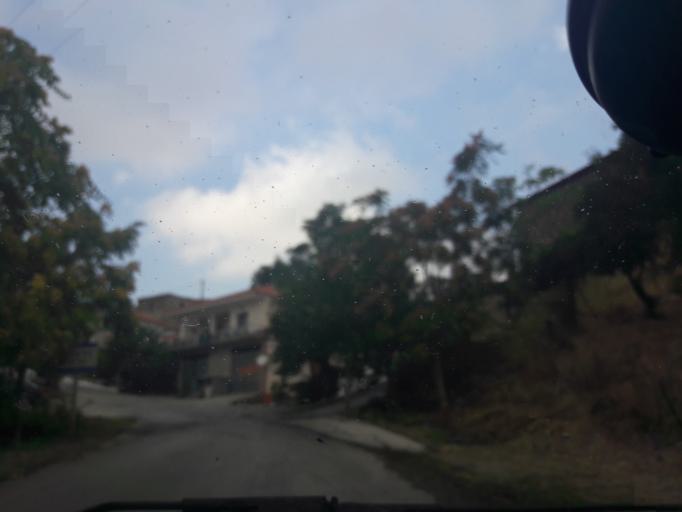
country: GR
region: North Aegean
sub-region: Nomos Lesvou
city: Myrina
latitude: 39.9489
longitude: 25.1660
